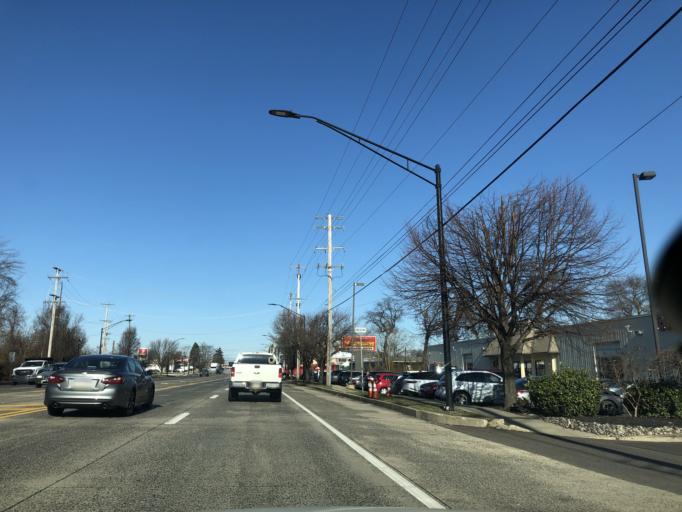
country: US
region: Pennsylvania
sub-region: Bucks County
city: Bristol
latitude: 40.1175
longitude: -74.8811
